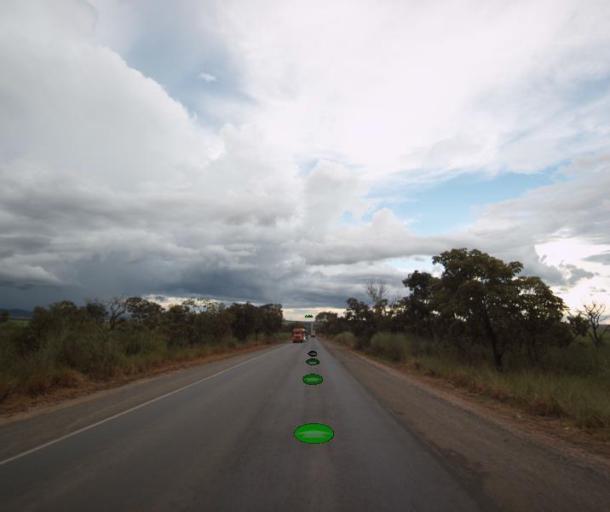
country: BR
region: Goias
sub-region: Itapaci
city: Itapaci
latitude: -14.8303
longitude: -49.3038
